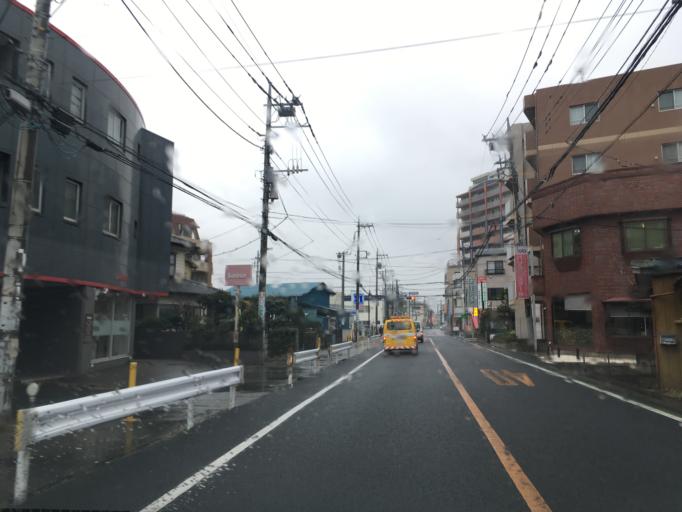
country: JP
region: Saitama
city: Koshigaya
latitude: 35.8864
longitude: 139.7840
